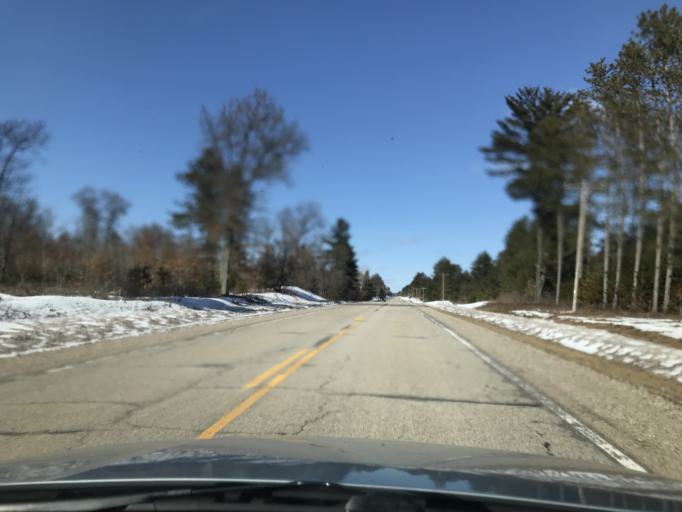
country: US
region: Wisconsin
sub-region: Marinette County
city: Niagara
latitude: 45.3839
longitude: -88.0997
